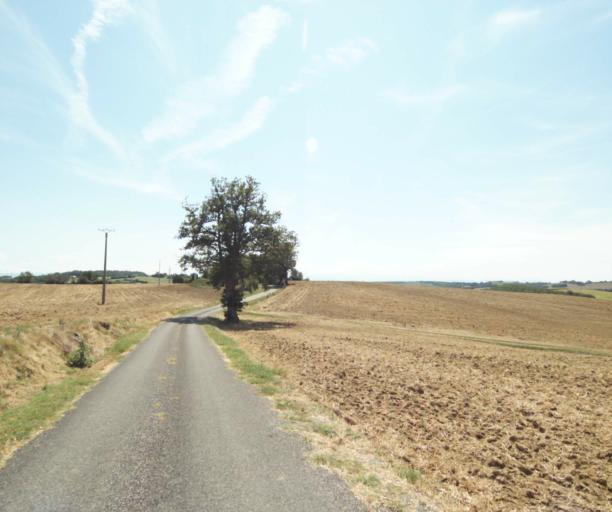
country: FR
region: Midi-Pyrenees
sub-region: Departement de l'Ariege
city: Lezat-sur-Leze
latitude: 43.2488
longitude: 1.3284
